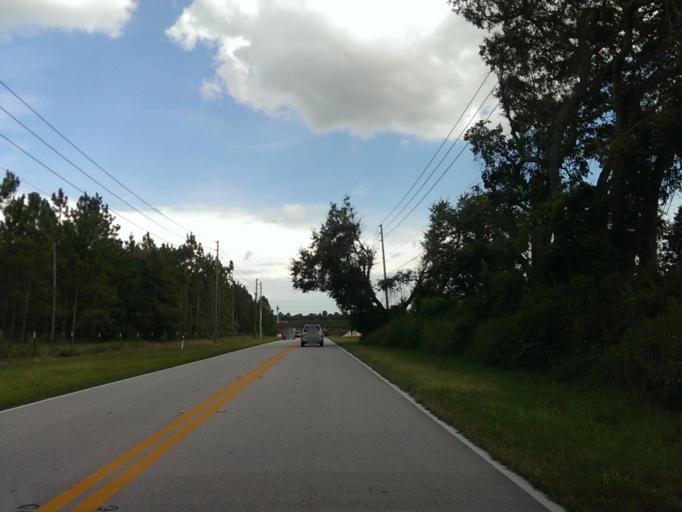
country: US
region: Florida
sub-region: Orange County
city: Oakland
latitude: 28.4616
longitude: -81.6391
